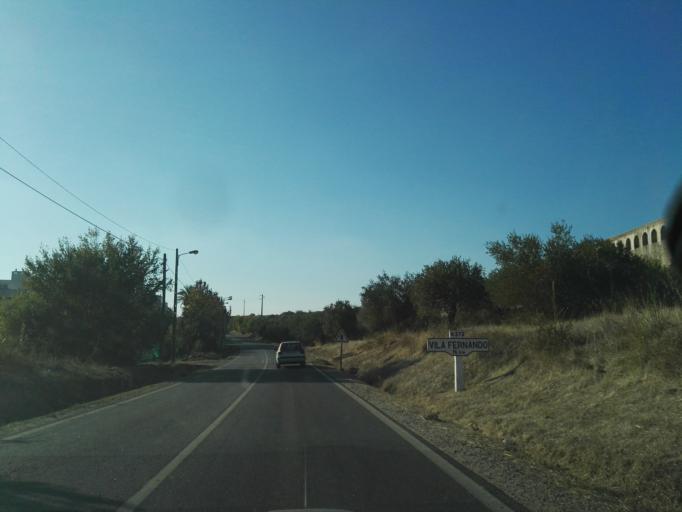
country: PT
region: Portalegre
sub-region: Elvas
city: Elvas
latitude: 38.8784
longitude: -7.1781
